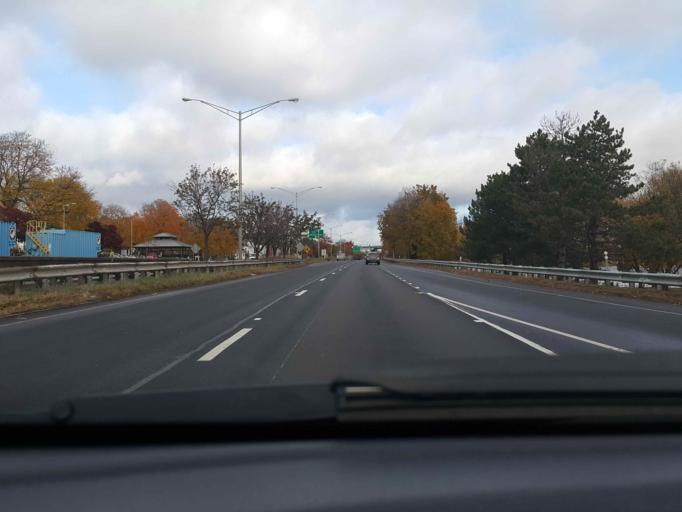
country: US
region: Connecticut
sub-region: Middlesex County
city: Middletown
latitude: 41.5610
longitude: -72.6464
